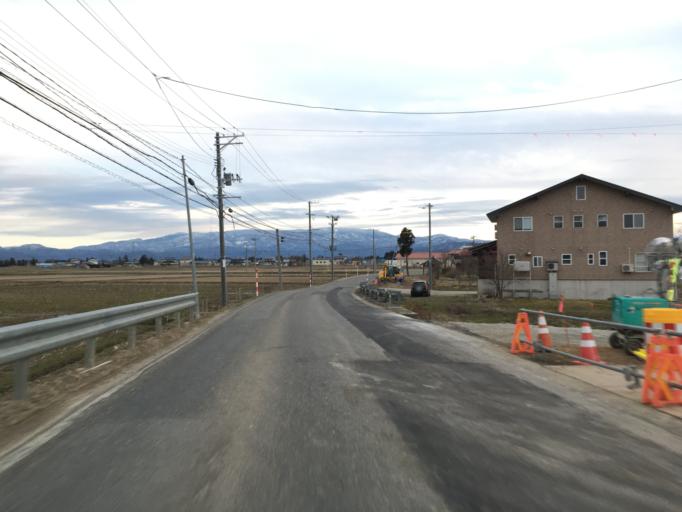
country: JP
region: Yamagata
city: Yonezawa
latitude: 37.9955
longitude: 140.0773
